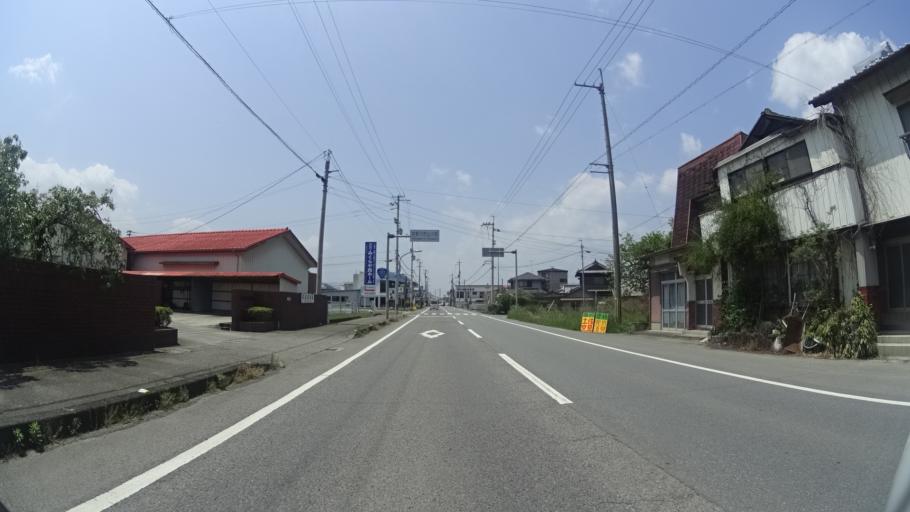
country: JP
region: Tokushima
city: Kamojimacho-jogejima
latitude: 34.0639
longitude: 134.2703
